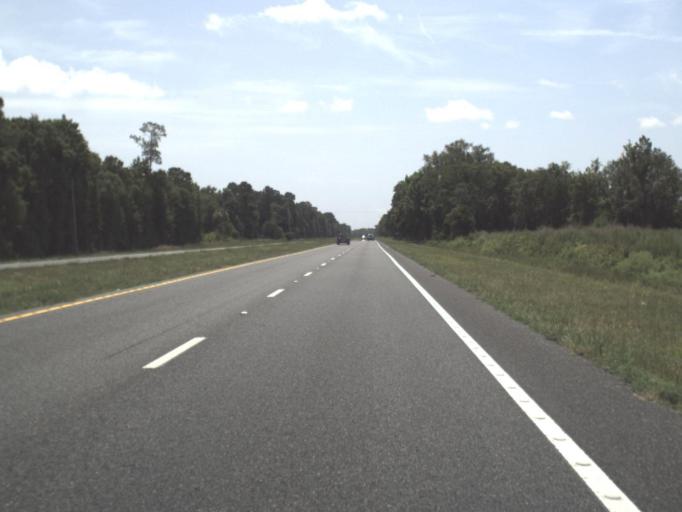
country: US
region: Florida
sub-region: Taylor County
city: Perry
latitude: 29.9781
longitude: -83.4875
